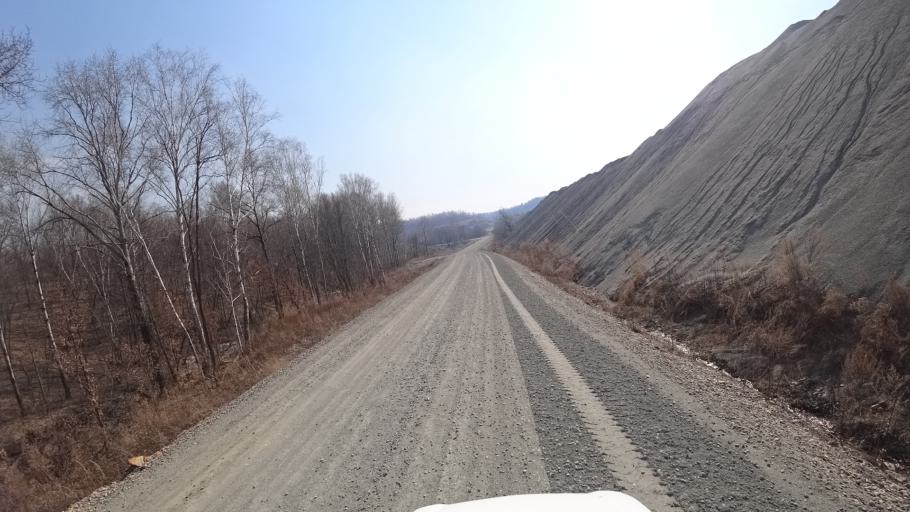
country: RU
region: Amur
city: Novobureyskiy
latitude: 49.7993
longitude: 129.9586
